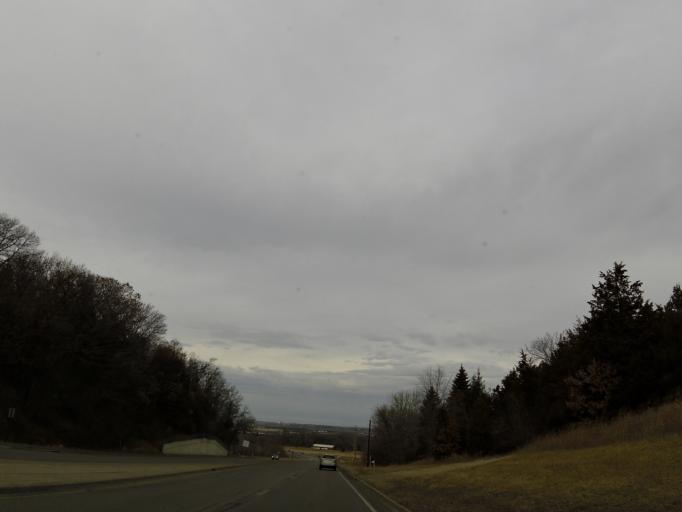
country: US
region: Minnesota
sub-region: Scott County
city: Prior Lake
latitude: 44.7634
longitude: -93.4034
